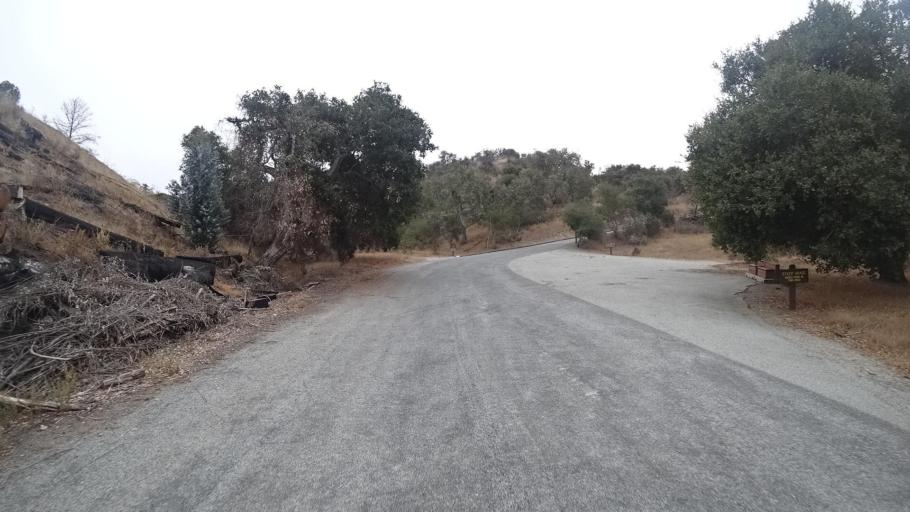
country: US
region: California
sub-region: Monterey County
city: Salinas
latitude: 36.5885
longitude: -121.6893
